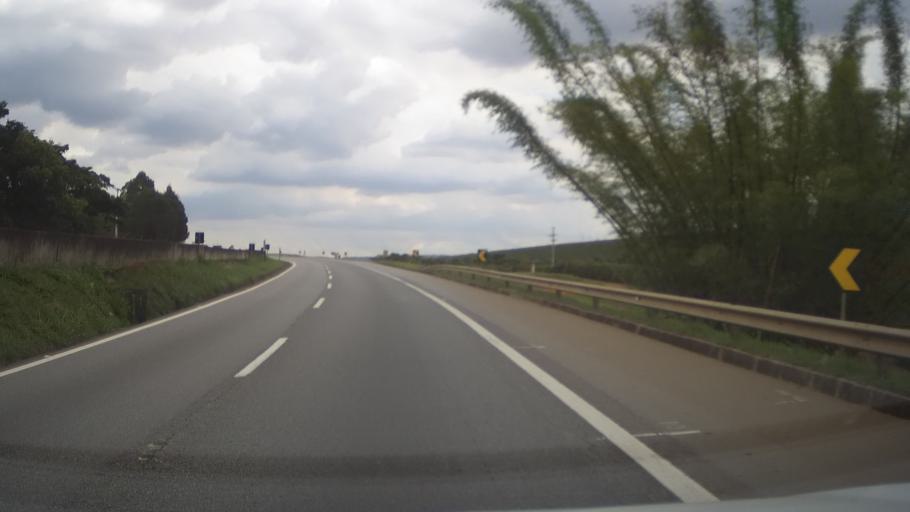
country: BR
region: Minas Gerais
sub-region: Tres Coracoes
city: Tres Coracoes
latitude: -21.5116
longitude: -45.2165
